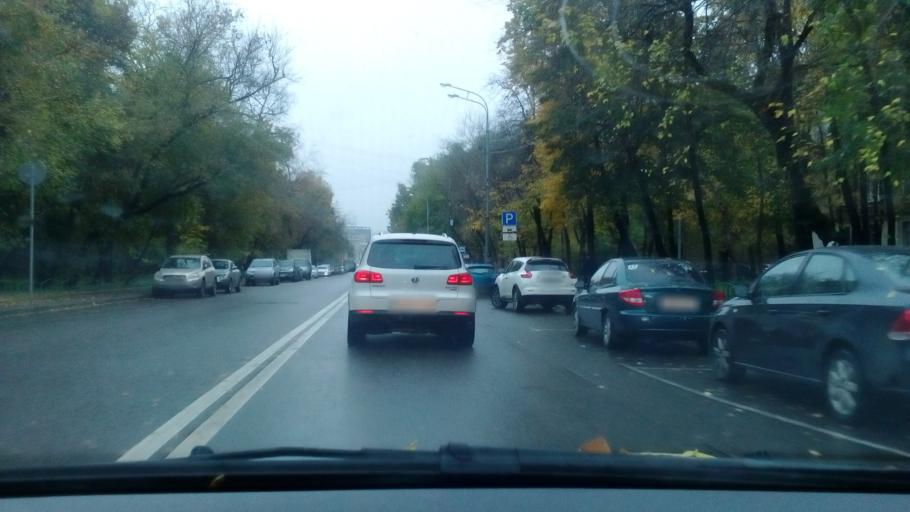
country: RU
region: Moscow
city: Mar'ina Roshcha
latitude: 55.7970
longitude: 37.5762
